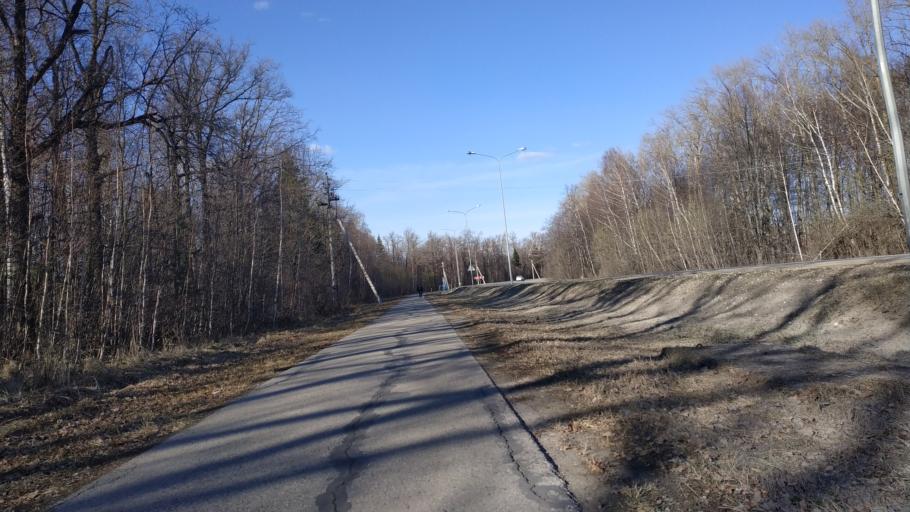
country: RU
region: Chuvashia
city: Ishley
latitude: 56.1298
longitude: 47.0715
